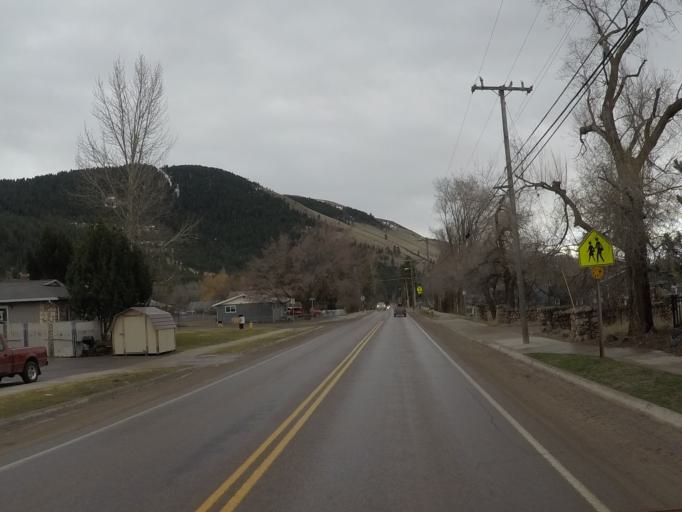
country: US
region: Montana
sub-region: Missoula County
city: East Missoula
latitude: 46.8935
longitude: -113.9657
